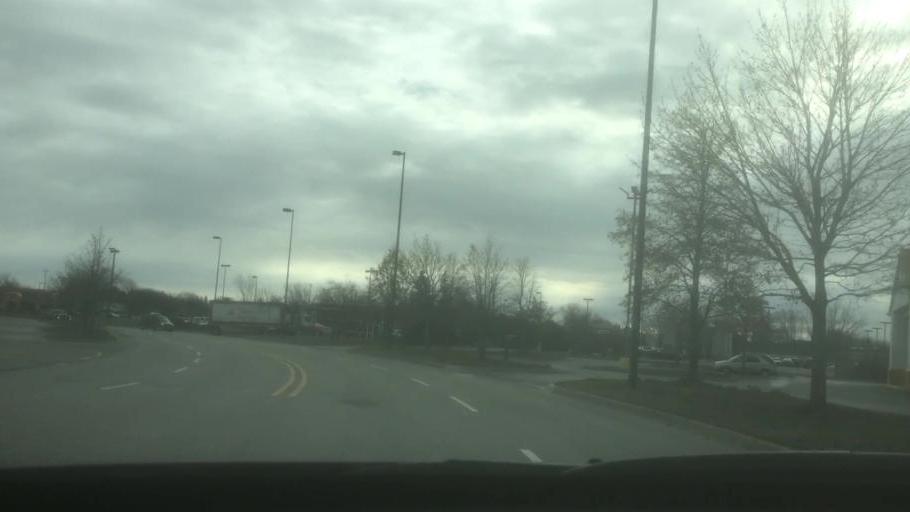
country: US
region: Michigan
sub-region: Bay County
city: Bay City
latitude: 43.6256
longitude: -83.8933
